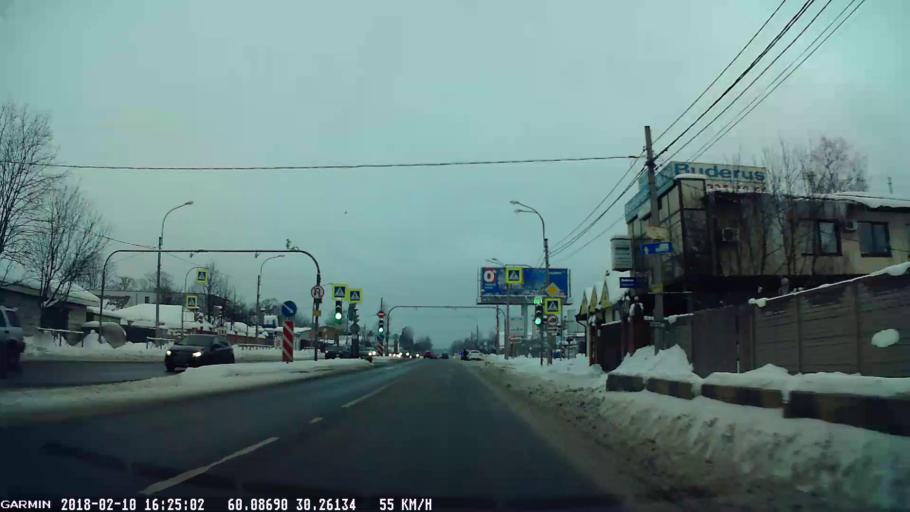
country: RU
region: St.-Petersburg
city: Pargolovo
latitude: 60.0877
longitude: 30.2608
